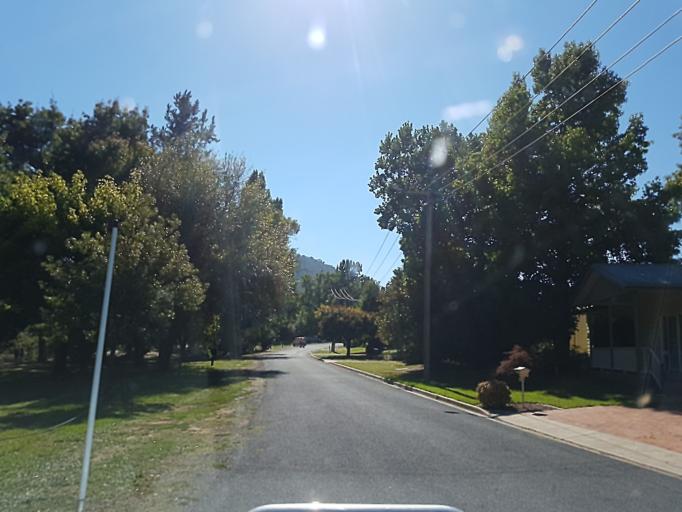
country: AU
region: Victoria
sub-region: Alpine
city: Mount Beauty
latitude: -36.7272
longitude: 146.9573
